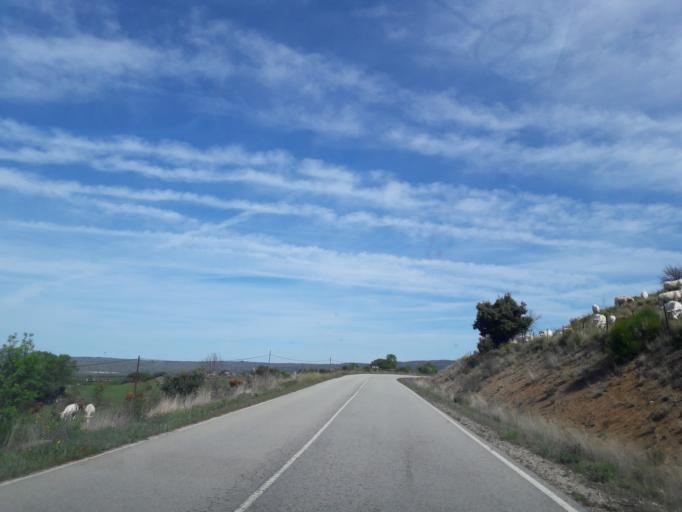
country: ES
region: Castille and Leon
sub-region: Provincia de Salamanca
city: Sanchotello
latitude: 40.4476
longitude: -5.7362
